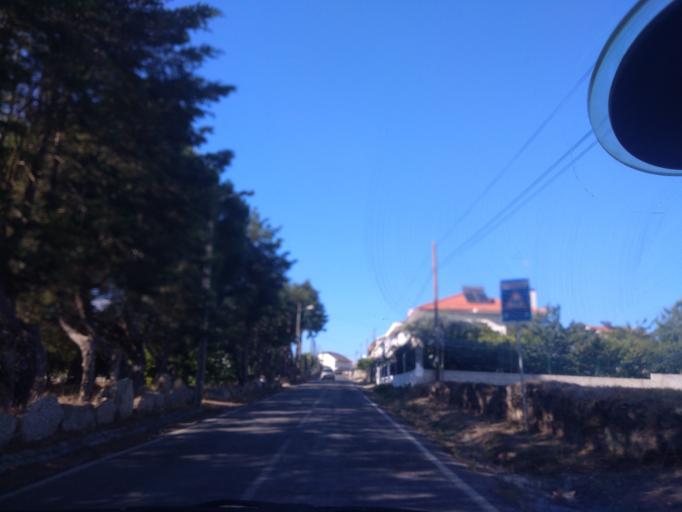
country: PT
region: Castelo Branco
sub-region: Covilha
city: Teixoso
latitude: 40.2559
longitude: -7.3936
